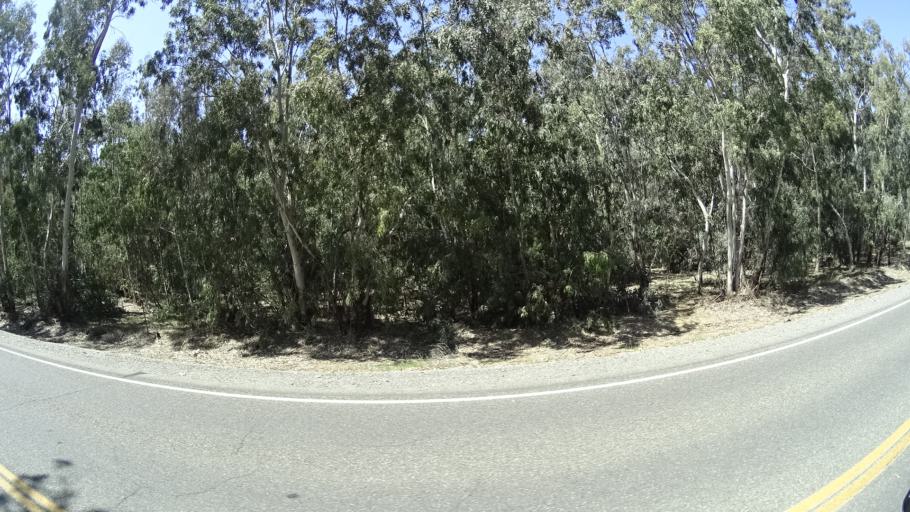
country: US
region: California
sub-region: Glenn County
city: Willows
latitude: 39.5959
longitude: -122.1942
